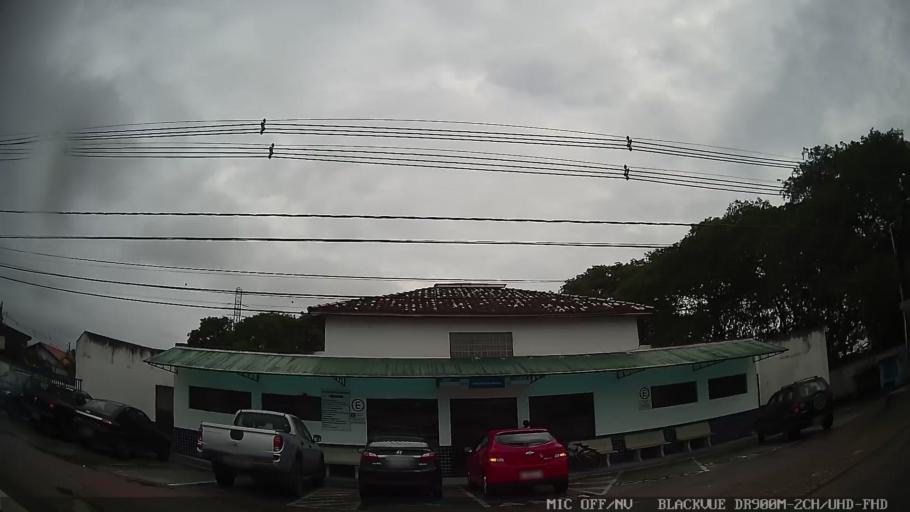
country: BR
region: Sao Paulo
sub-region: Sao Sebastiao
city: Sao Sebastiao
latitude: -23.6916
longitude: -45.4436
